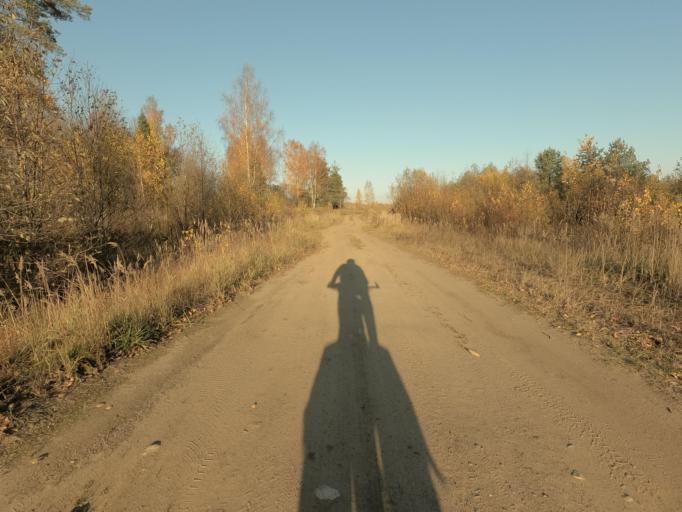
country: RU
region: Leningrad
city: Kirovsk
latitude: 59.8601
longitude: 31.0081
